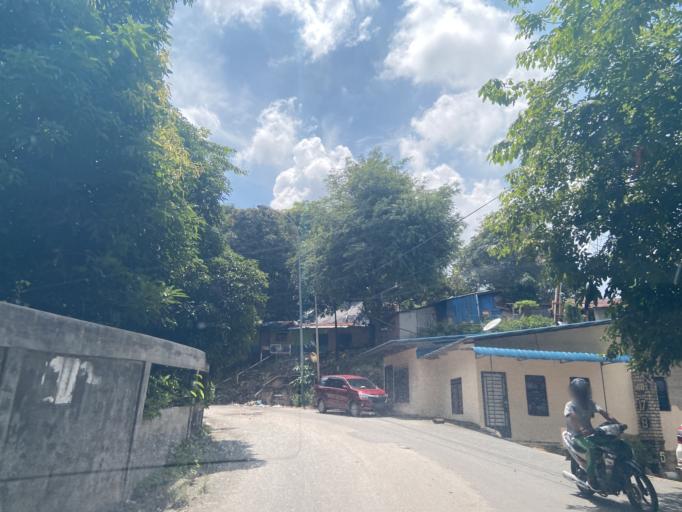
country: SG
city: Singapore
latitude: 1.1539
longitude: 104.0140
